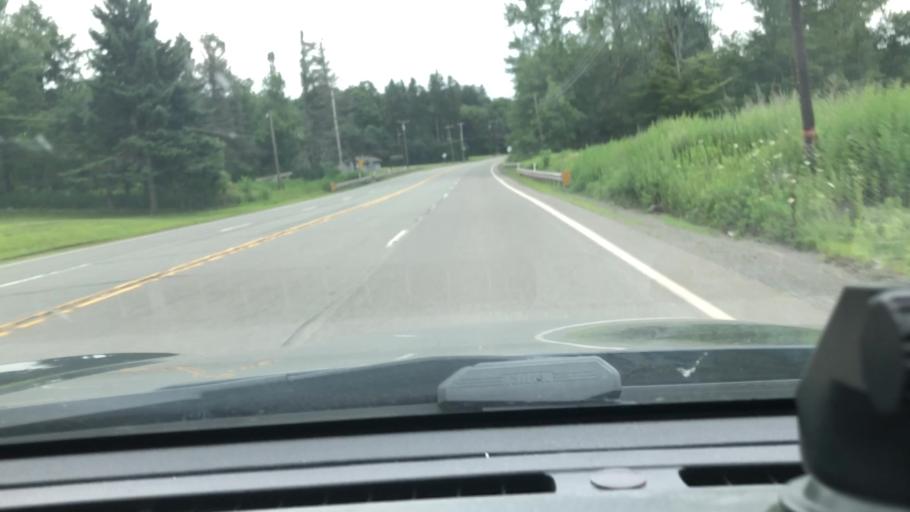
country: US
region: Pennsylvania
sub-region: Lackawanna County
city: Moscow
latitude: 41.2469
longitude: -75.5025
